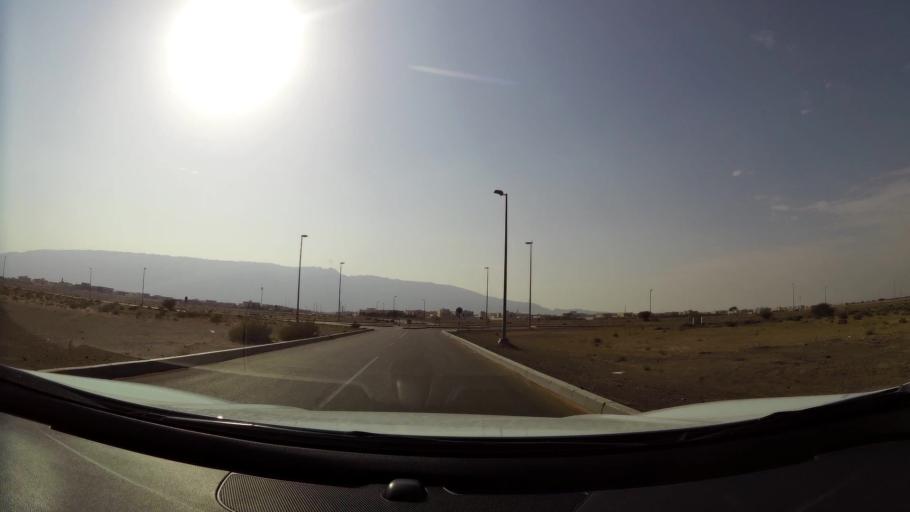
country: AE
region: Abu Dhabi
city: Al Ain
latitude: 24.0751
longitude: 55.8608
